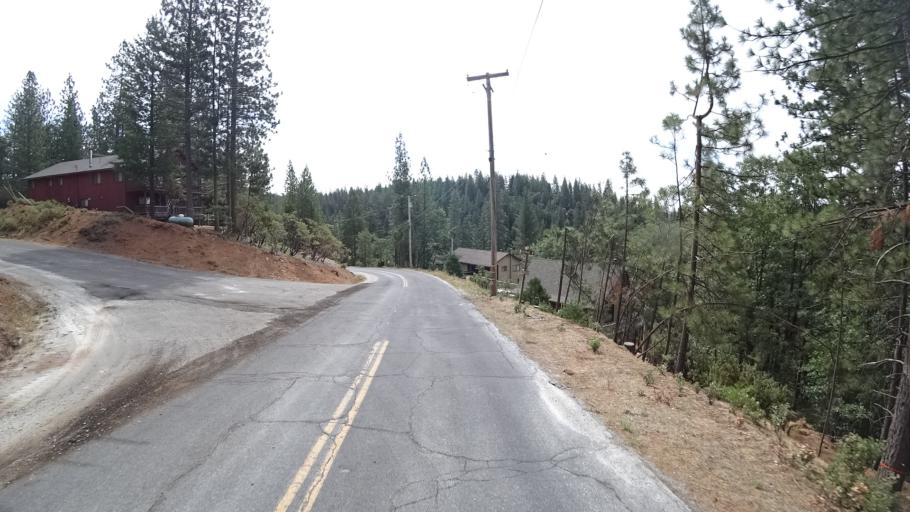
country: US
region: California
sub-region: Calaveras County
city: Arnold
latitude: 38.2437
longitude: -120.3432
